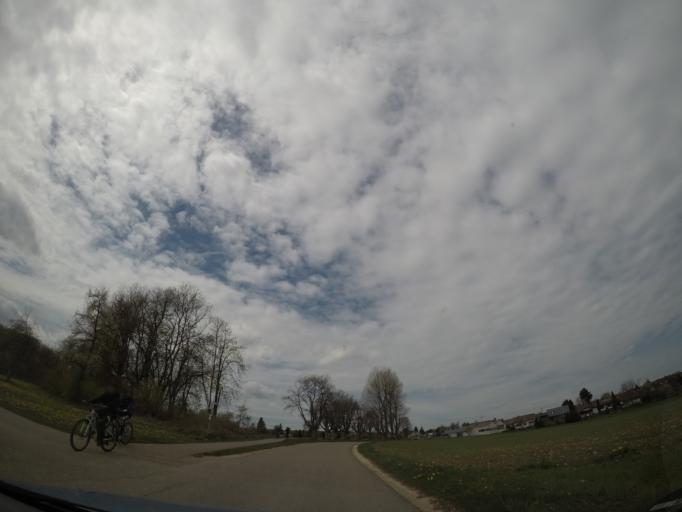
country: DE
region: Baden-Wuerttemberg
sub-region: Tuebingen Region
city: Laichingen
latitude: 48.4818
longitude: 9.6873
